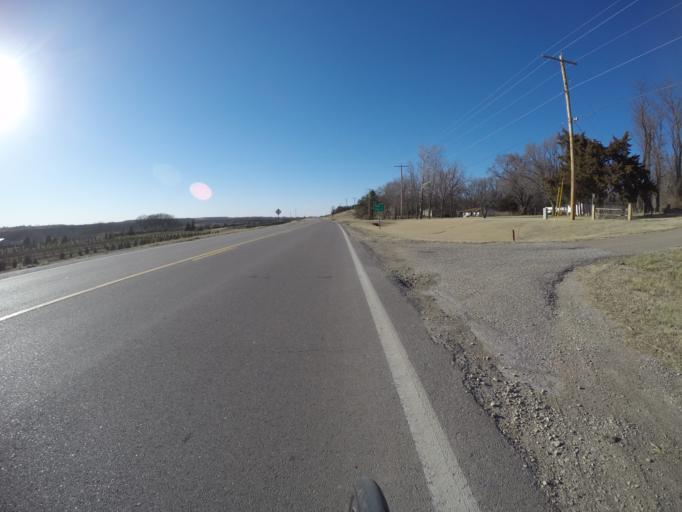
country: US
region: Kansas
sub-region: Riley County
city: Manhattan
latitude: 39.1950
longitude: -96.6460
